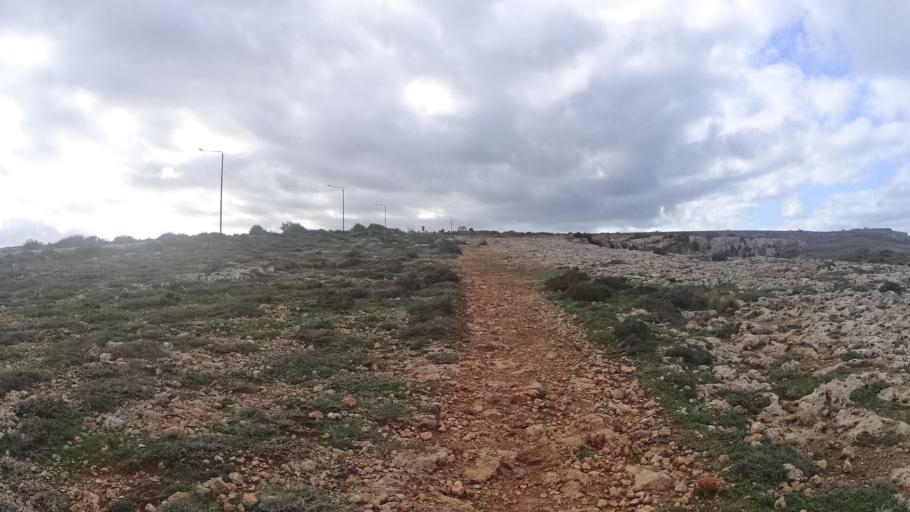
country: MT
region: Il-Mellieha
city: Mellieha
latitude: 35.9835
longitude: 14.3348
